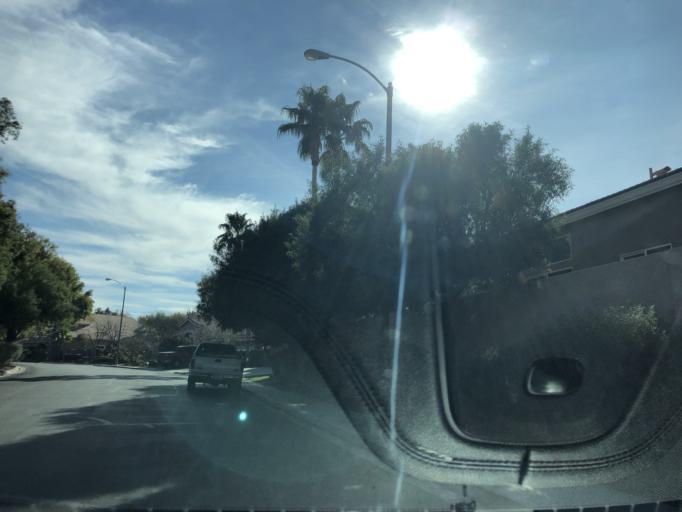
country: US
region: Nevada
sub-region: Clark County
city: Whitney
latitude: 36.0164
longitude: -115.0799
